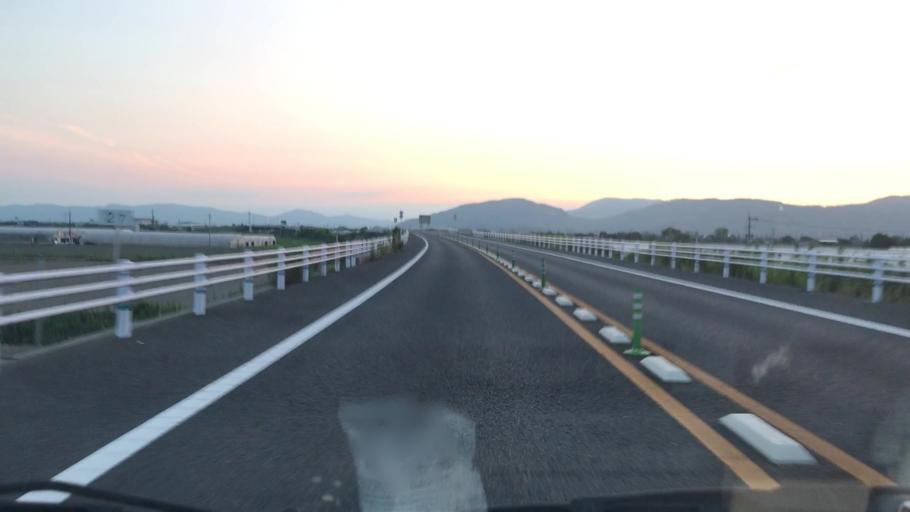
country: JP
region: Saga Prefecture
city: Saga-shi
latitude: 33.2306
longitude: 130.2289
